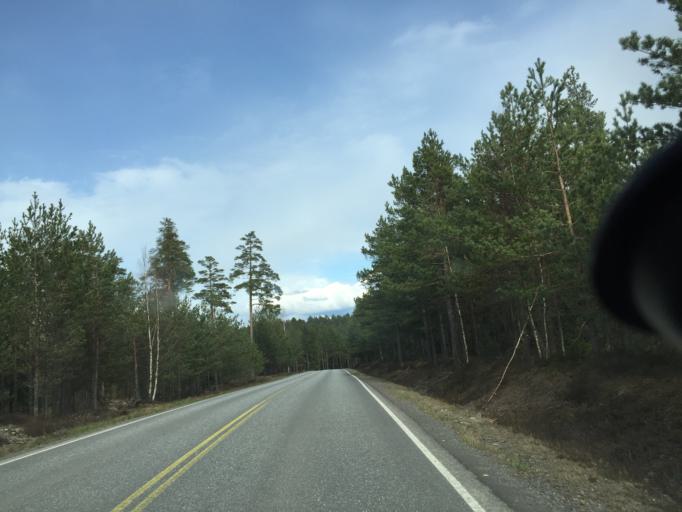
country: FI
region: Varsinais-Suomi
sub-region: Salo
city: Saerkisalo
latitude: 59.9990
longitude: 23.0803
